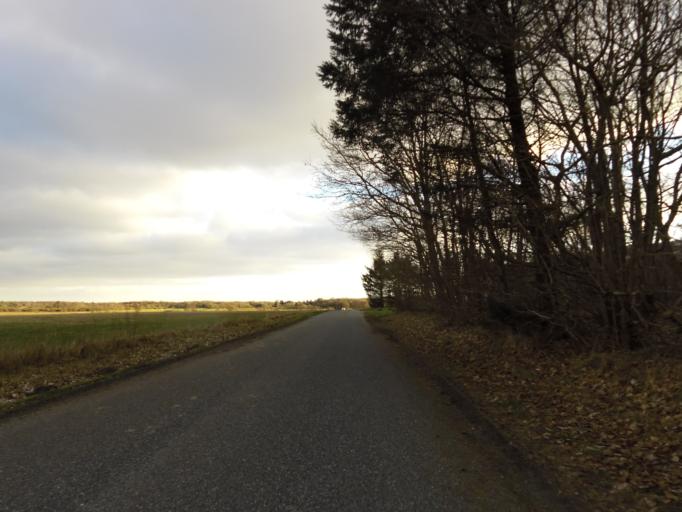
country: DK
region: South Denmark
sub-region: Esbjerg Kommune
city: Ribe
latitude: 55.2996
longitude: 8.8496
